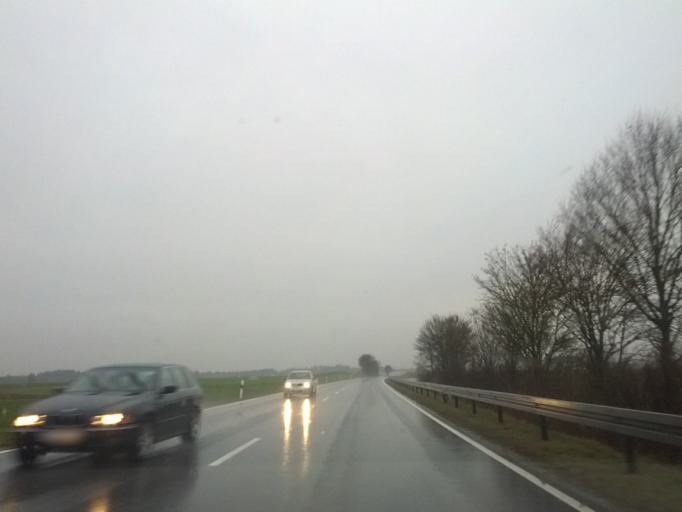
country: DE
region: Baden-Wuerttemberg
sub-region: Tuebingen Region
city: Ochsenhausen
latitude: 48.0697
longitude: 9.9304
